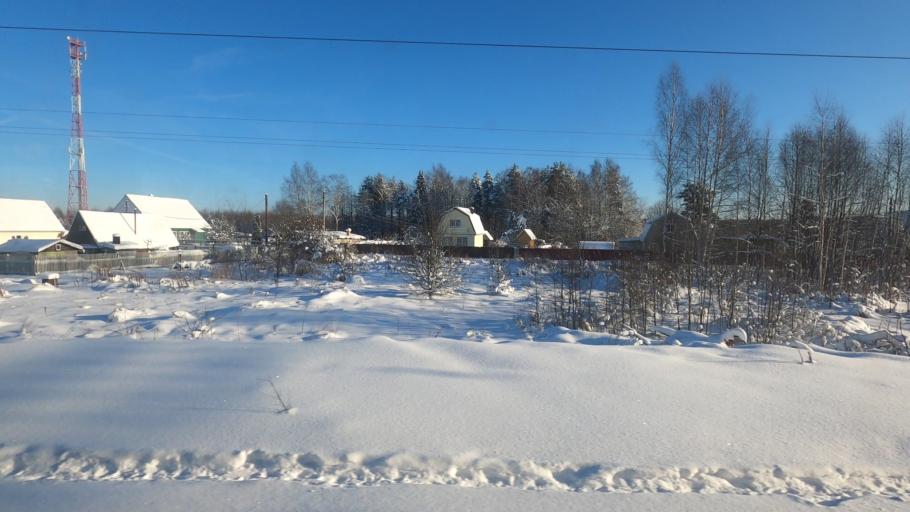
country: RU
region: Moskovskaya
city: Novo-Nikol'skoye
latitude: 56.6432
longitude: 37.5624
